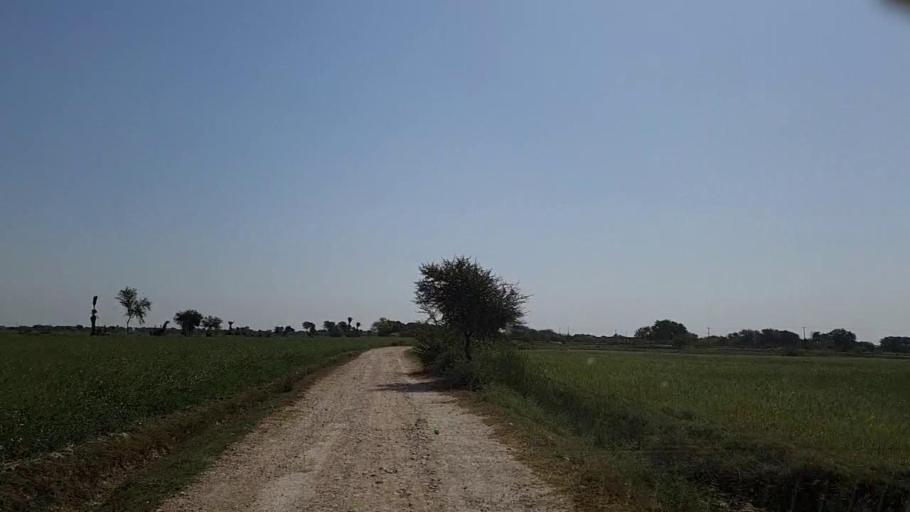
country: PK
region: Sindh
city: Mirpur Batoro
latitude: 24.6815
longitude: 68.2927
